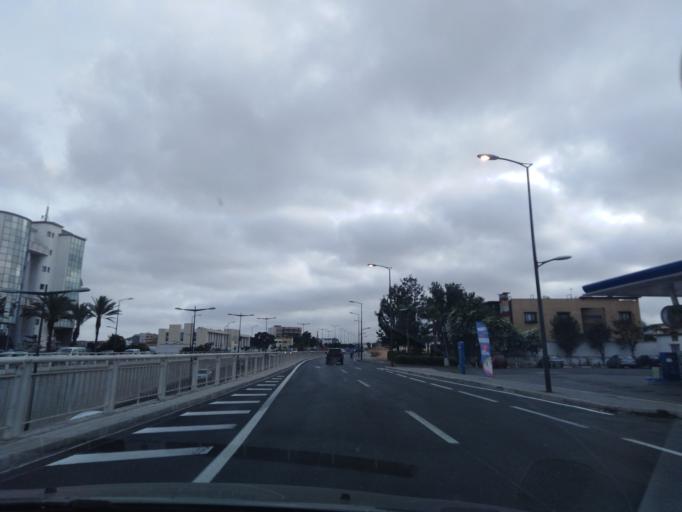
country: MA
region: Grand Casablanca
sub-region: Casablanca
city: Casablanca
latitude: 33.5375
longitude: -7.6643
